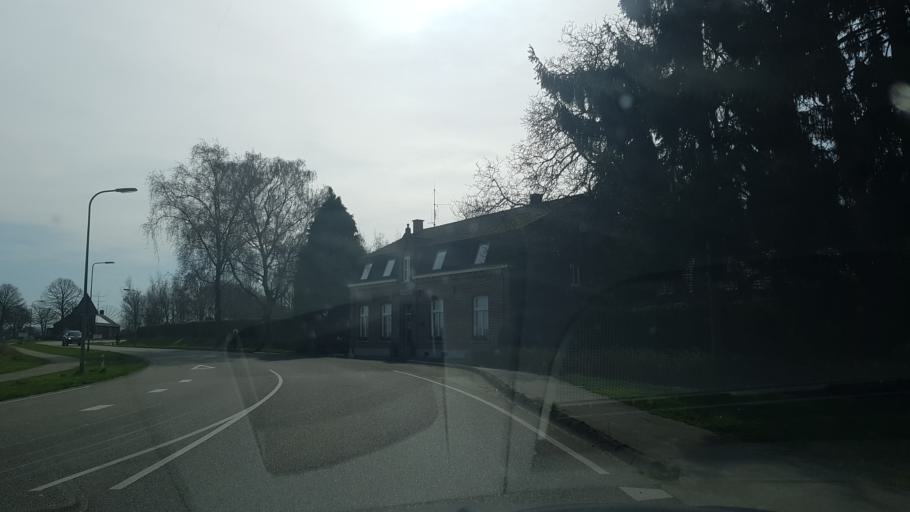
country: NL
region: Limburg
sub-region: Gemeente Leudal
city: Kelpen-Oler
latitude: 51.1697
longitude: 5.8248
